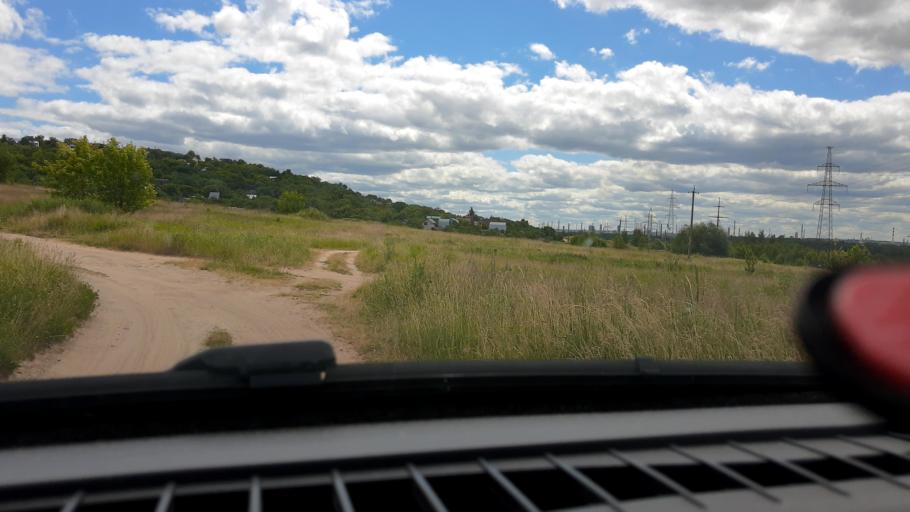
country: RU
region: Nizjnij Novgorod
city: Kstovo
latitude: 56.1419
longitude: 44.1704
